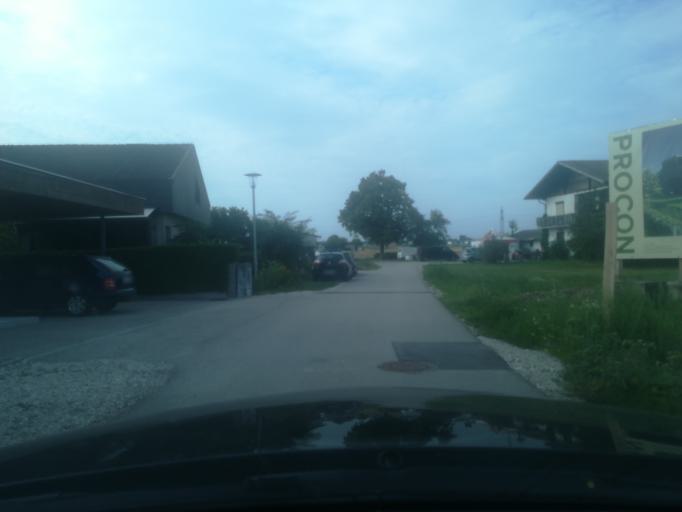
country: AT
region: Upper Austria
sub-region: Wels-Land
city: Marchtrenk
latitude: 48.2000
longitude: 14.1208
